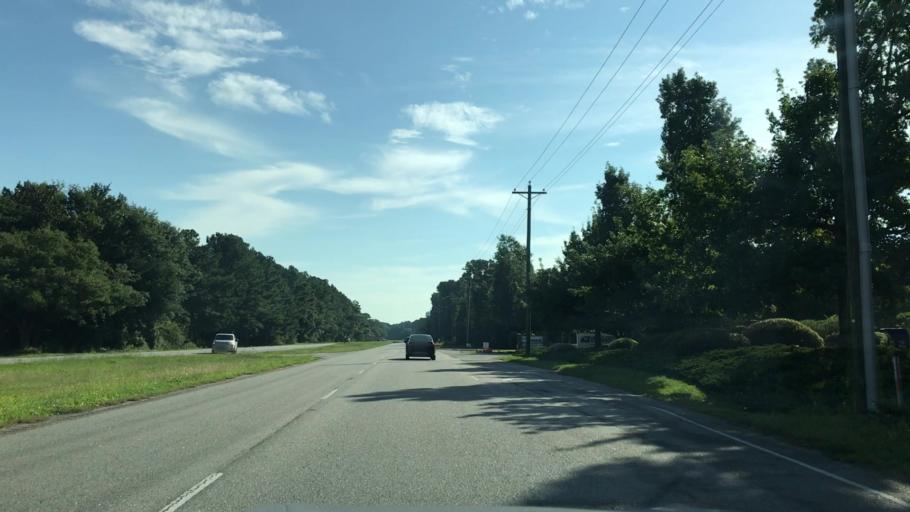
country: US
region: South Carolina
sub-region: Charleston County
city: Awendaw
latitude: 32.9822
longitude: -79.6579
